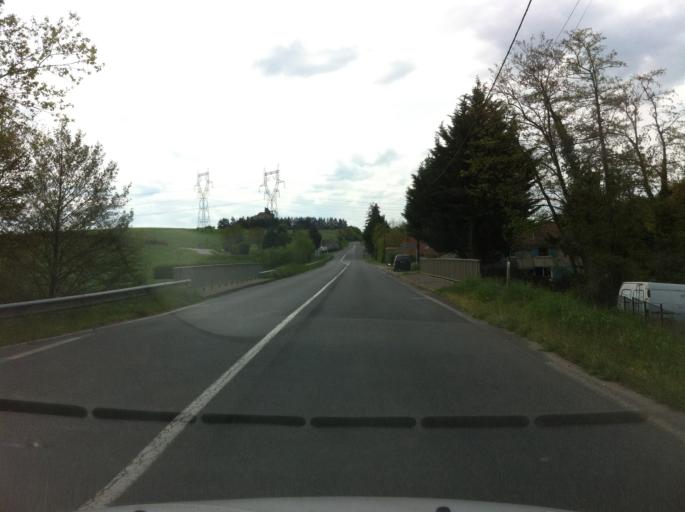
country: FR
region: Auvergne
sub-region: Departement de l'Allier
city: Saint-Pourcain-sur-Sioule
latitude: 46.3149
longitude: 3.2623
